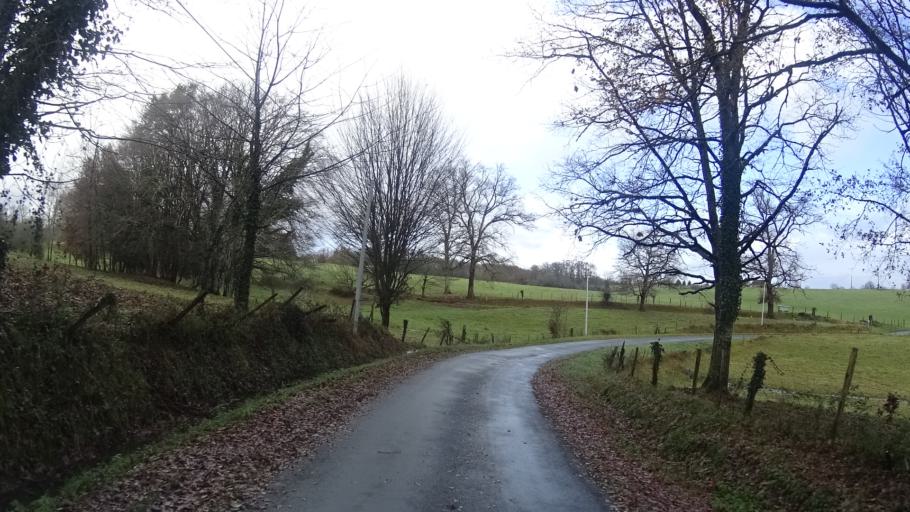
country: FR
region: Aquitaine
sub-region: Departement de la Dordogne
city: Thiviers
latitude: 45.4105
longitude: 0.9673
